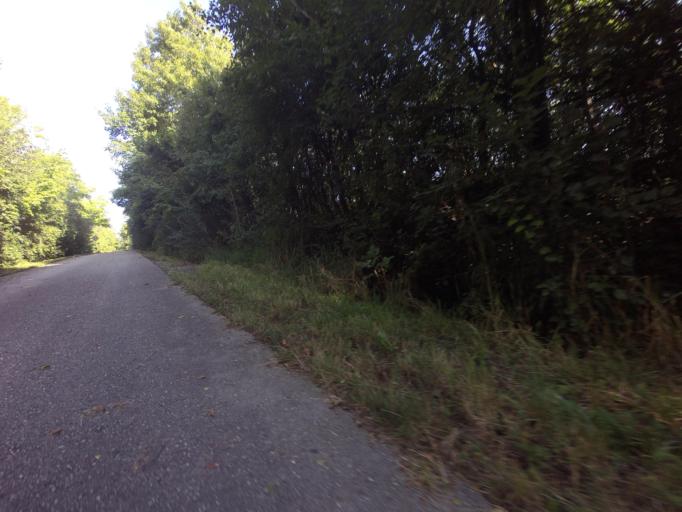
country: CA
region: Ontario
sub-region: Wellington County
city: Guelph
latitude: 43.6528
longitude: -80.4188
